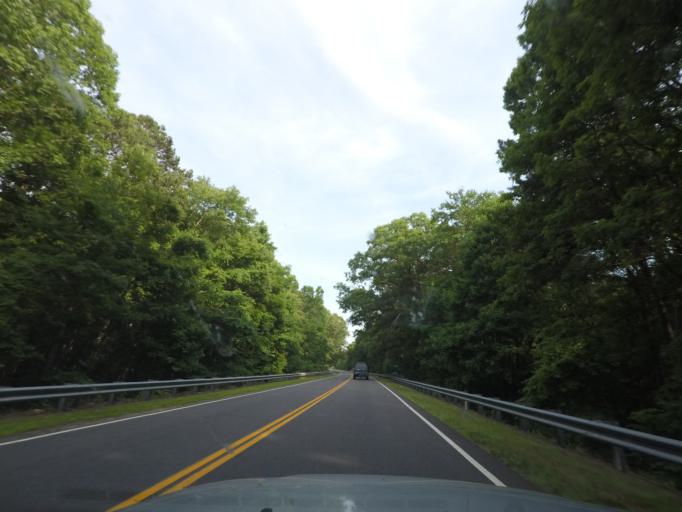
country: US
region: Virginia
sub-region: Mecklenburg County
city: Clarksville
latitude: 36.6971
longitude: -78.6267
